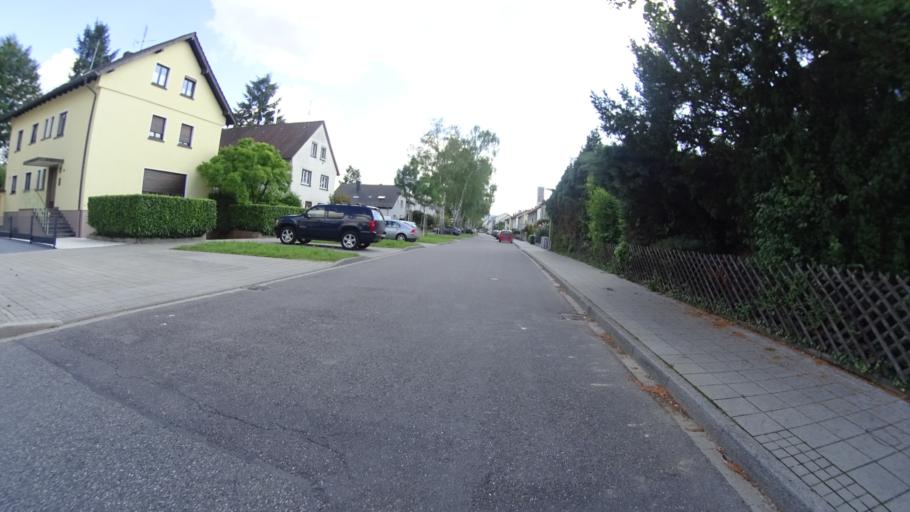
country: DE
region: Baden-Wuerttemberg
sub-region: Karlsruhe Region
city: Karlsruhe
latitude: 48.9904
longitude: 8.4627
